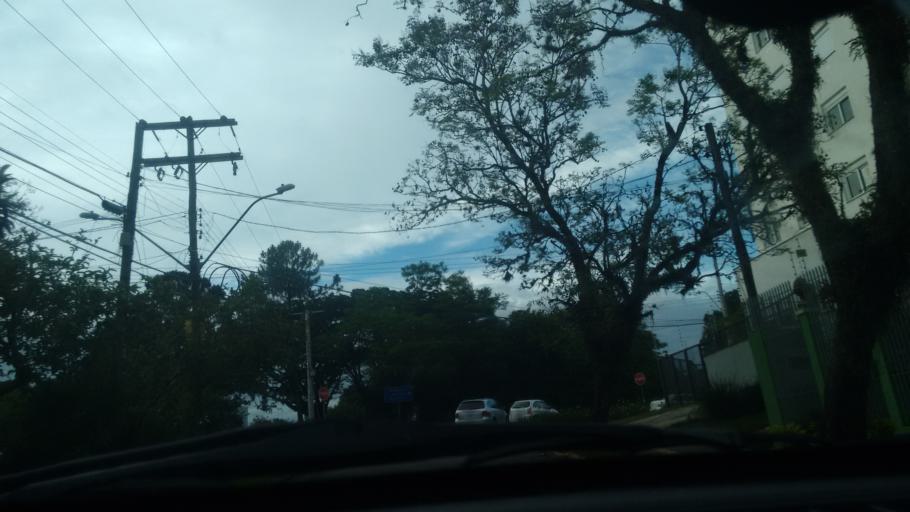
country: BR
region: Rio Grande do Sul
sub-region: Cachoeirinha
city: Cachoeirinha
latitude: -30.0037
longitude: -51.1458
